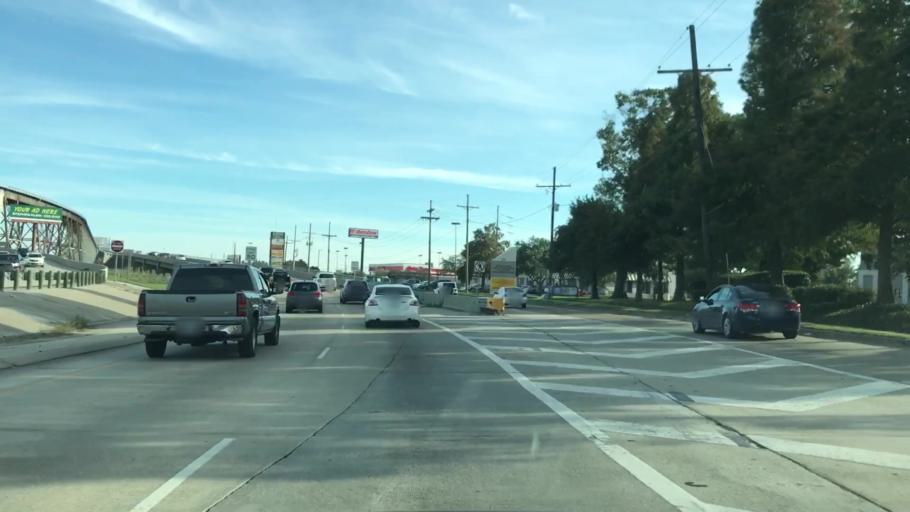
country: US
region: Louisiana
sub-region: Jefferson Parish
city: Elmwood
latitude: 29.9556
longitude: -90.1822
